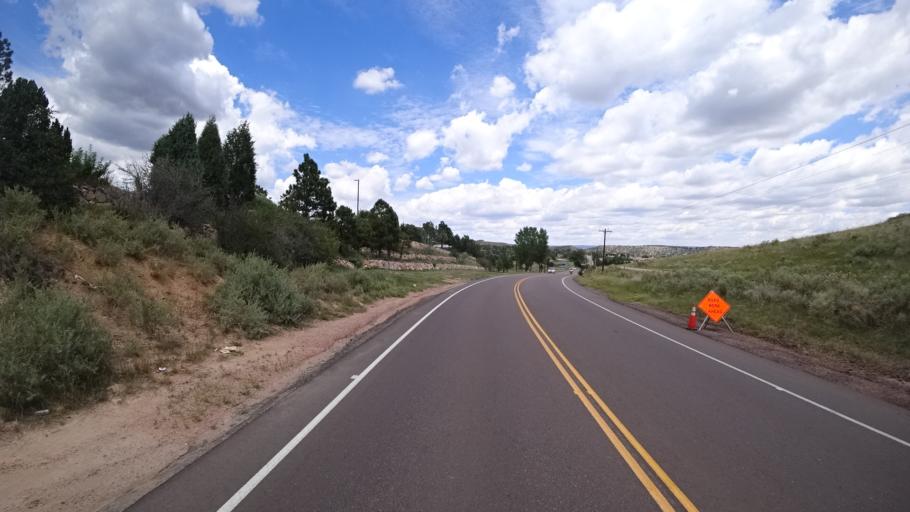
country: US
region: Colorado
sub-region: El Paso County
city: Manitou Springs
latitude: 38.8955
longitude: -104.8750
